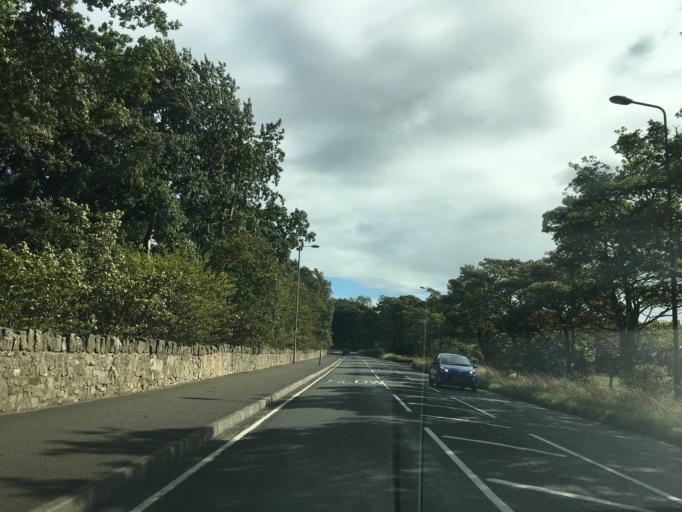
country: GB
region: Scotland
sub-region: Midlothian
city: Loanhead
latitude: 55.8990
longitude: -3.1839
